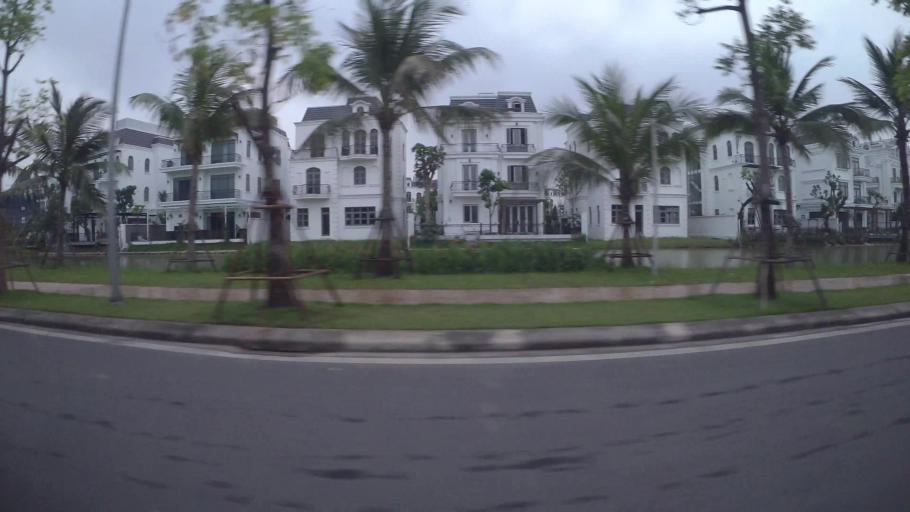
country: VN
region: Ha Noi
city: Trau Quy
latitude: 21.0414
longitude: 105.9085
